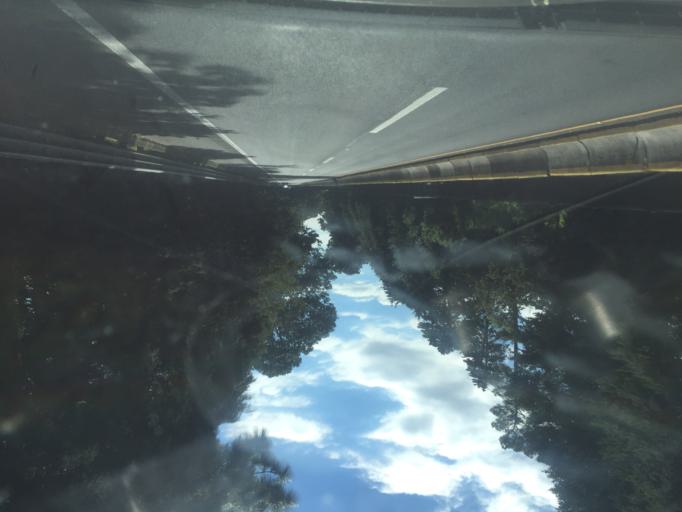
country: MX
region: Morelos
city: Tres Marias
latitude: 19.0425
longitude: -99.2327
